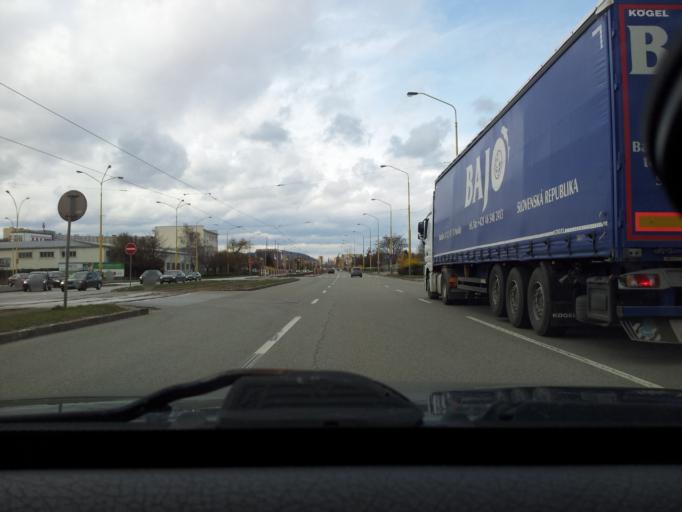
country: SK
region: Kosicky
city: Kosice
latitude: 48.6943
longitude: 21.2649
